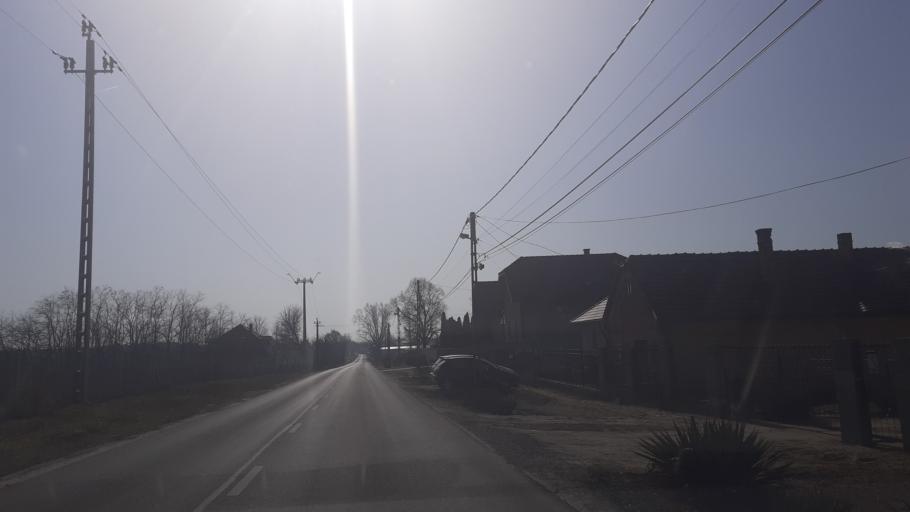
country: HU
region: Pest
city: Dabas
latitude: 47.1630
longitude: 19.3329
